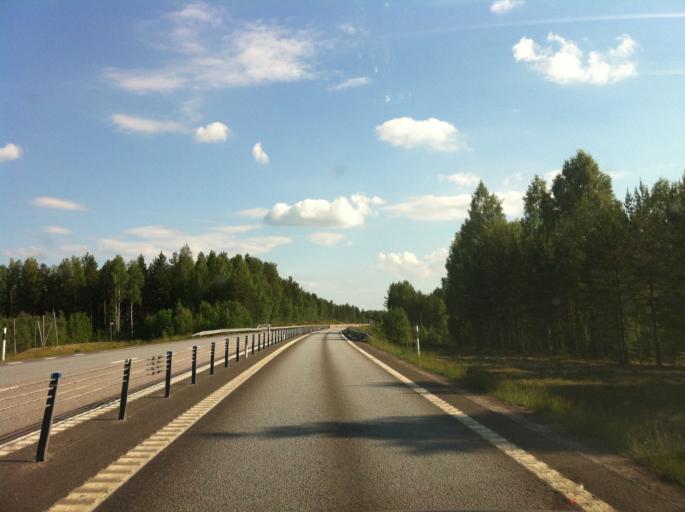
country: SE
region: Vaermland
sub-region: Kils Kommun
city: Kil
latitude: 59.4671
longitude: 13.3703
